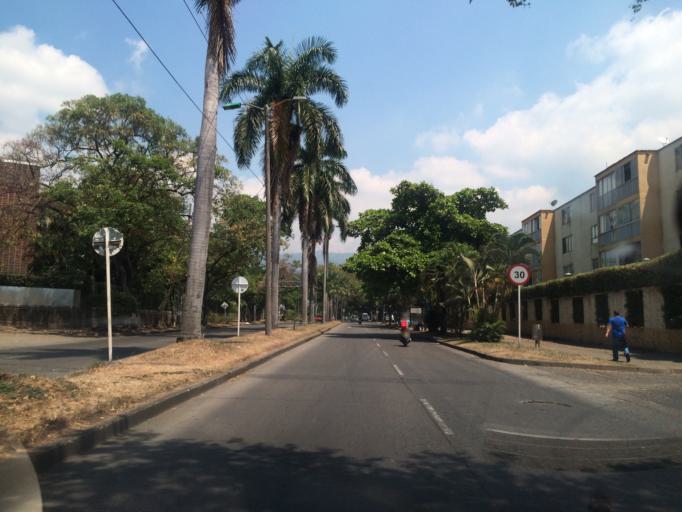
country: CO
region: Valle del Cauca
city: Cali
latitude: 3.4069
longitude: -76.5407
